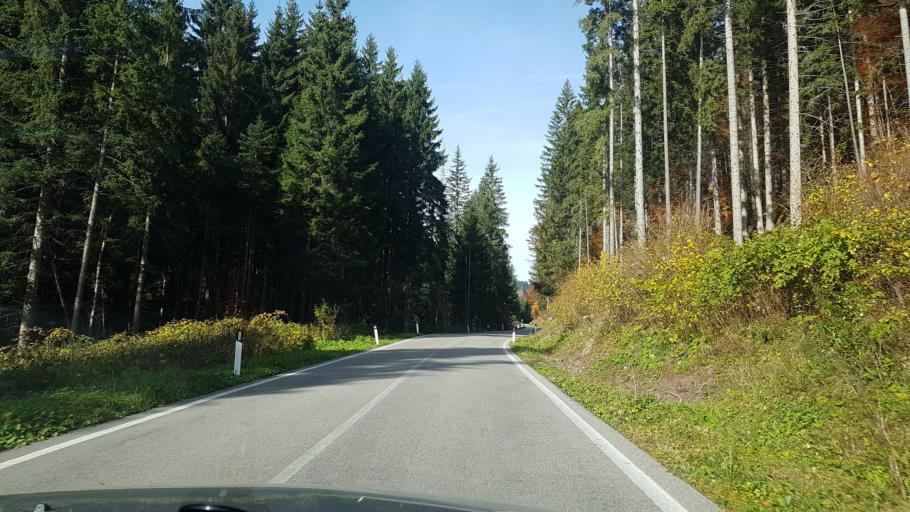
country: IT
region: Veneto
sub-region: Provincia di Belluno
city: Candide
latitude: 46.6343
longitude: 12.4628
